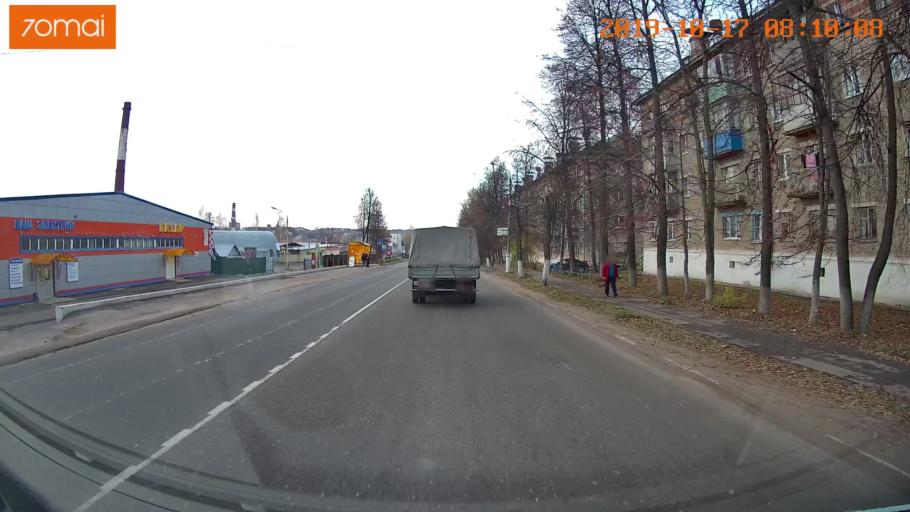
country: RU
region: Vladimir
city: Kol'chugino
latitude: 56.3093
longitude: 39.3786
